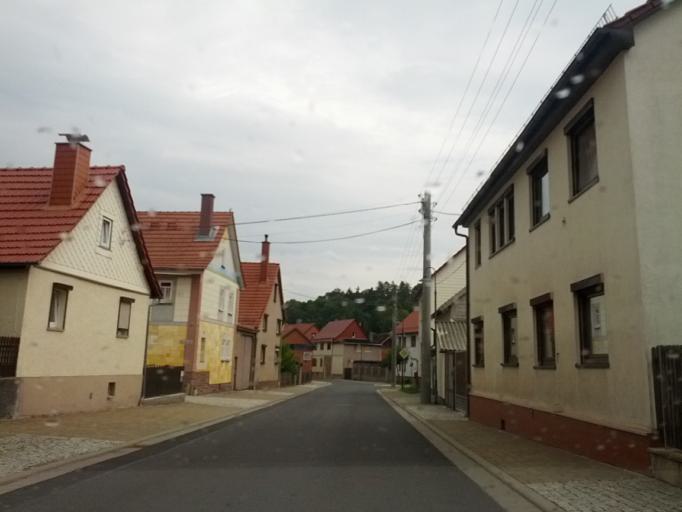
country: DE
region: Thuringia
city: Ernstroda
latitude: 50.8629
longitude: 10.6141
